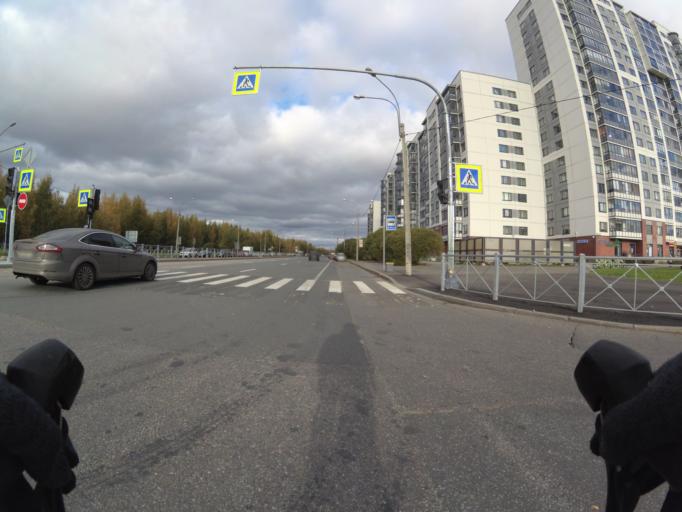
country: RU
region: Leningrad
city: Untolovo
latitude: 60.0032
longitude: 30.1956
